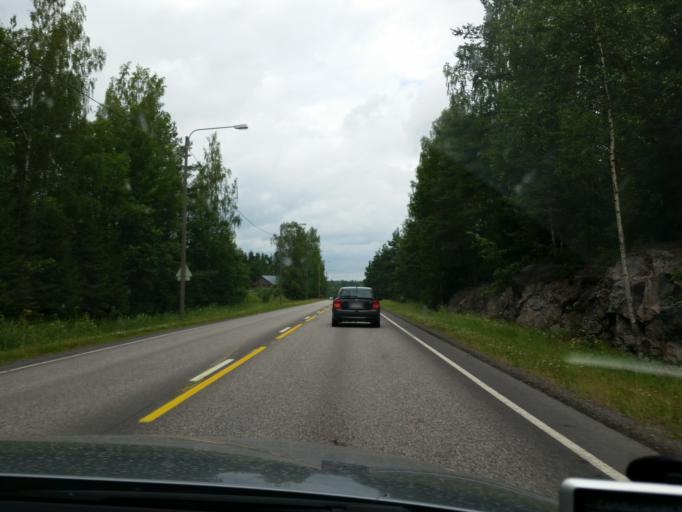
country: FI
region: Uusimaa
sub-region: Helsinki
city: Vihti
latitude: 60.3489
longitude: 24.1889
